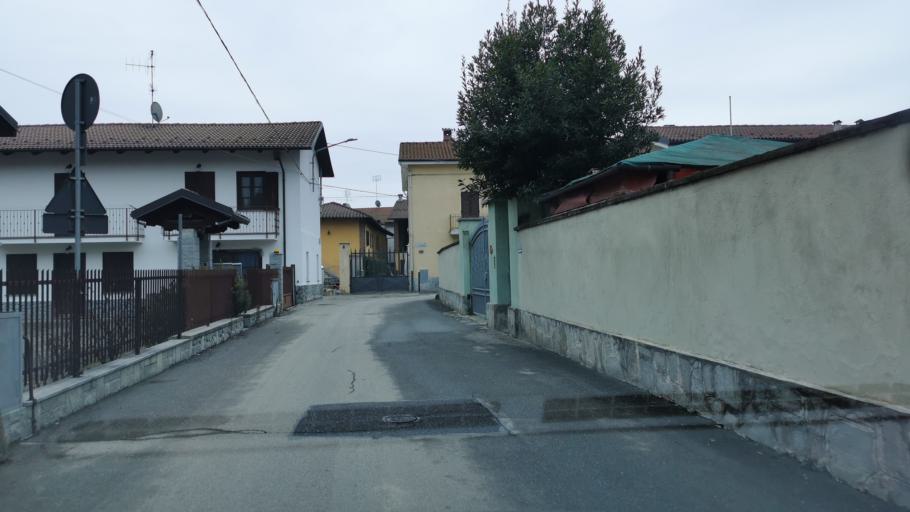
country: IT
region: Piedmont
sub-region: Provincia di Torino
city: Front
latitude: 45.2650
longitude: 7.6906
